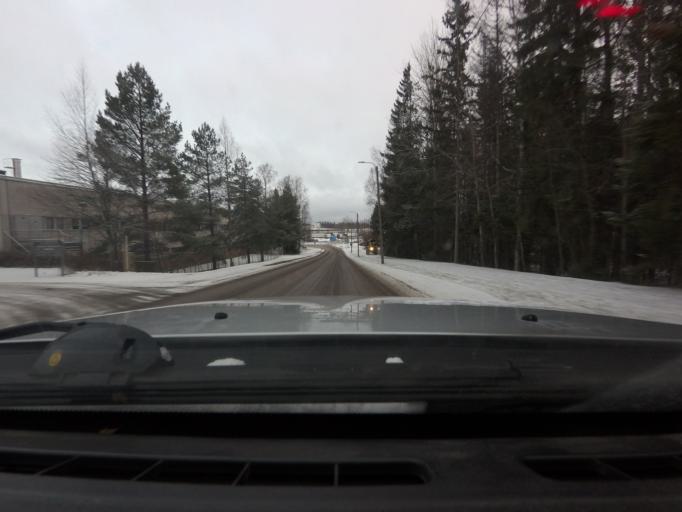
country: FI
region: Uusimaa
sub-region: Helsinki
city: Kauniainen
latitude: 60.2135
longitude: 24.7524
